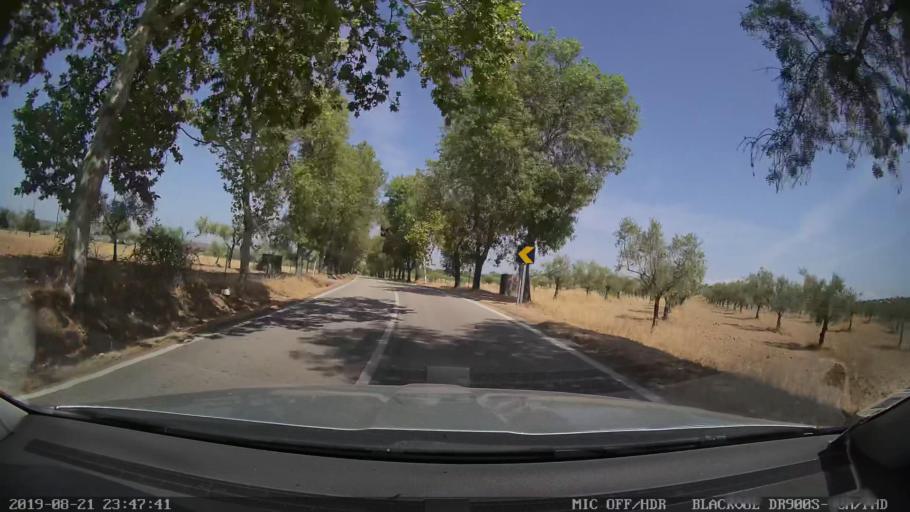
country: PT
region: Castelo Branco
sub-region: Idanha-A-Nova
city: Idanha-a-Nova
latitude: 39.8551
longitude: -7.2578
